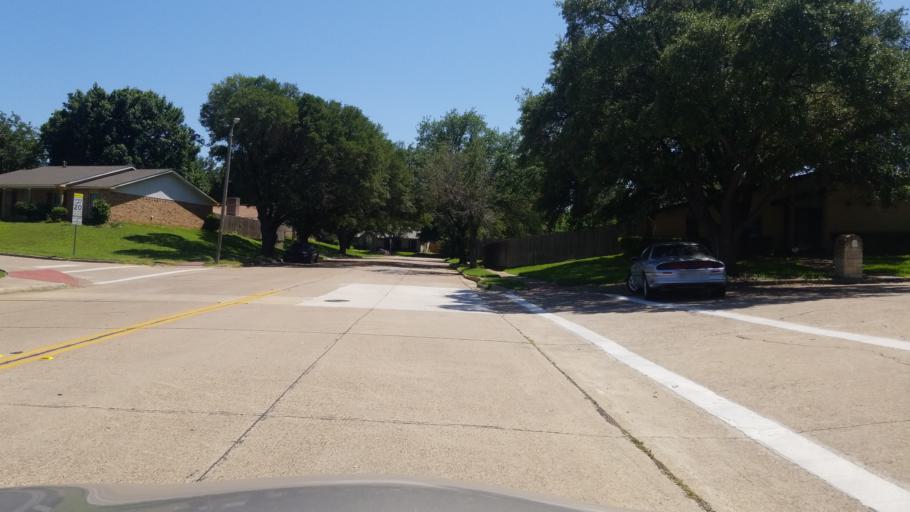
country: US
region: Texas
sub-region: Dallas County
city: Grand Prairie
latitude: 32.6929
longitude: -96.9938
